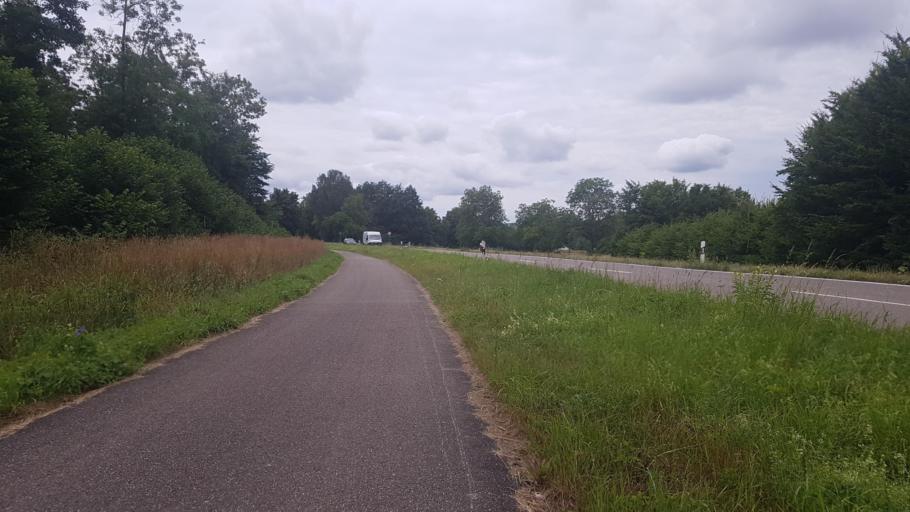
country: DE
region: Baden-Wuerttemberg
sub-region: Karlsruhe Region
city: Steinmauern
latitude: 48.8852
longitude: 8.2079
